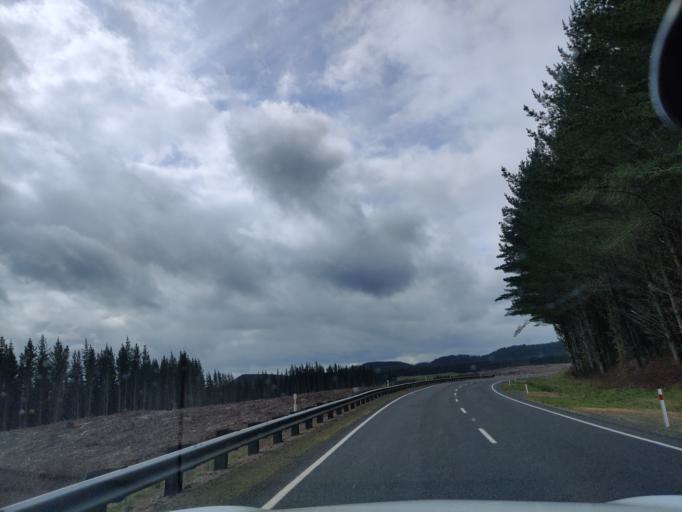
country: NZ
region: Waikato
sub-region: South Waikato District
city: Tokoroa
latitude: -38.3265
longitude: 175.8202
